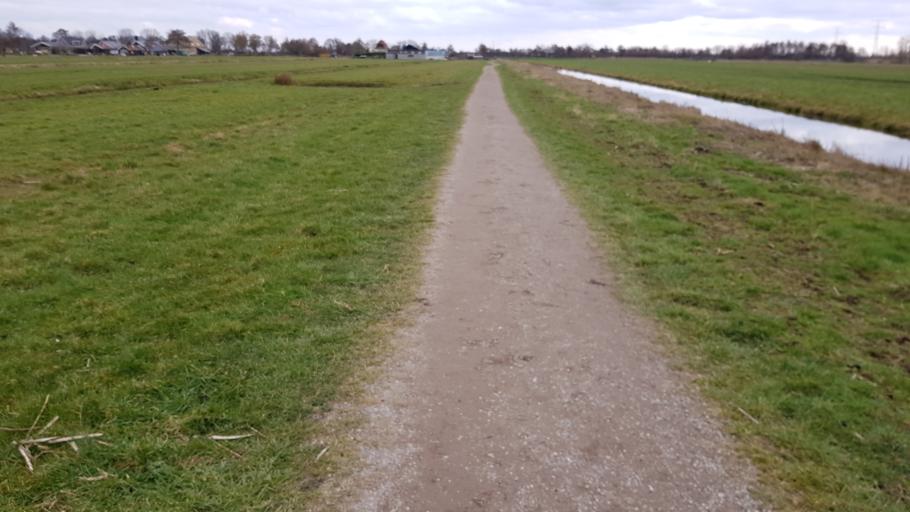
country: NL
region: South Holland
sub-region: Molenwaard
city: Nieuw-Lekkerland
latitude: 51.9231
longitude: 4.6578
